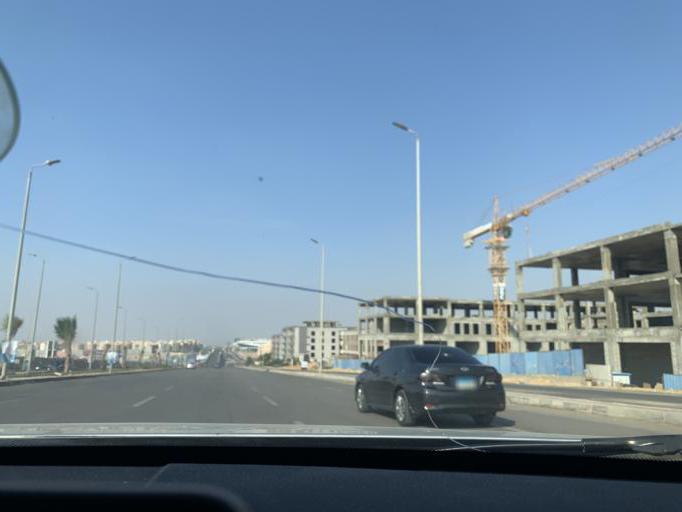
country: EG
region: Muhafazat al Qalyubiyah
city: Al Khankah
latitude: 30.0198
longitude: 31.4750
